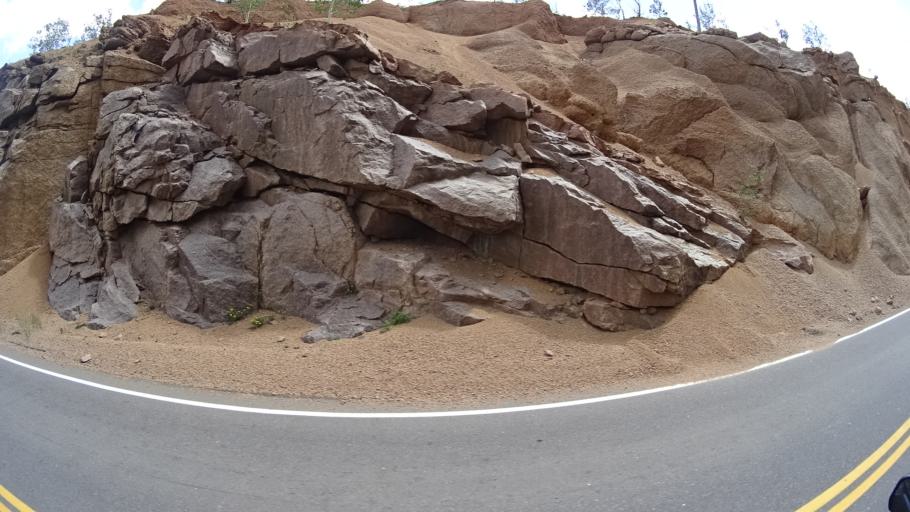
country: US
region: Colorado
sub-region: El Paso County
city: Cascade-Chipita Park
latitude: 38.9187
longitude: -105.0226
